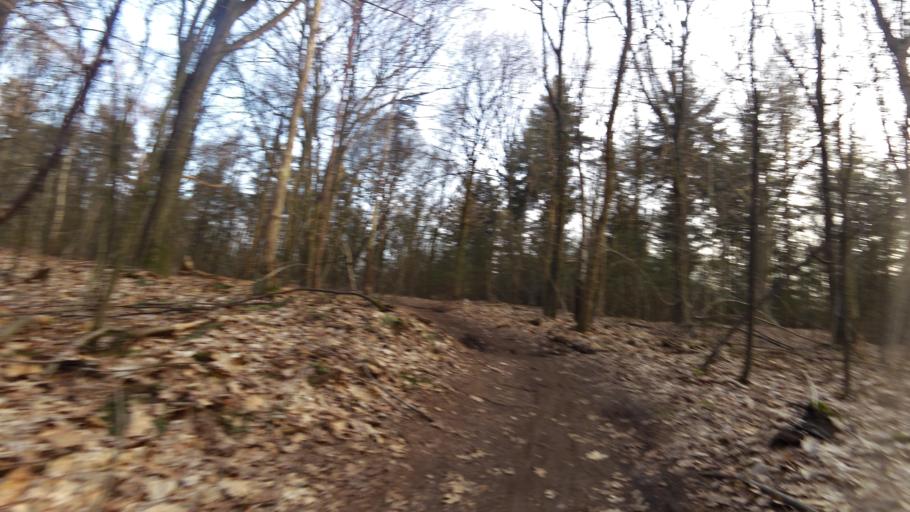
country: NL
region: Gelderland
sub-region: Gemeente Ede
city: Lunteren
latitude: 52.1023
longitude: 5.6471
